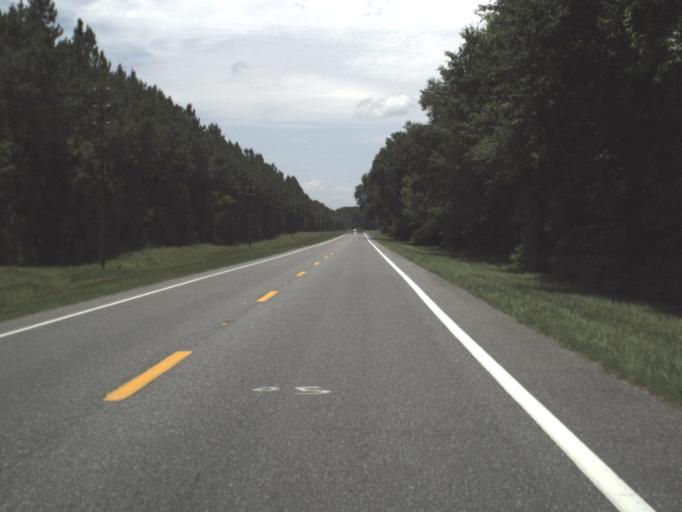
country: US
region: Florida
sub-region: Lafayette County
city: Mayo
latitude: 30.1291
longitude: -83.1690
